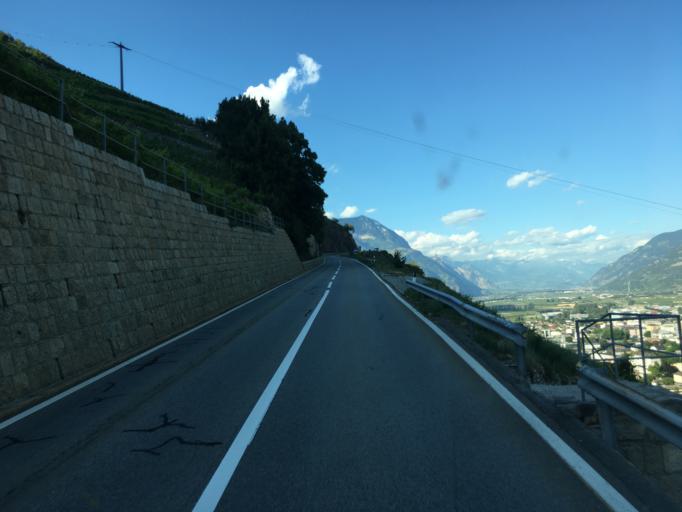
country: CH
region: Valais
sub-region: Martigny District
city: Martigny-Ville
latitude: 46.0979
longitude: 7.0595
